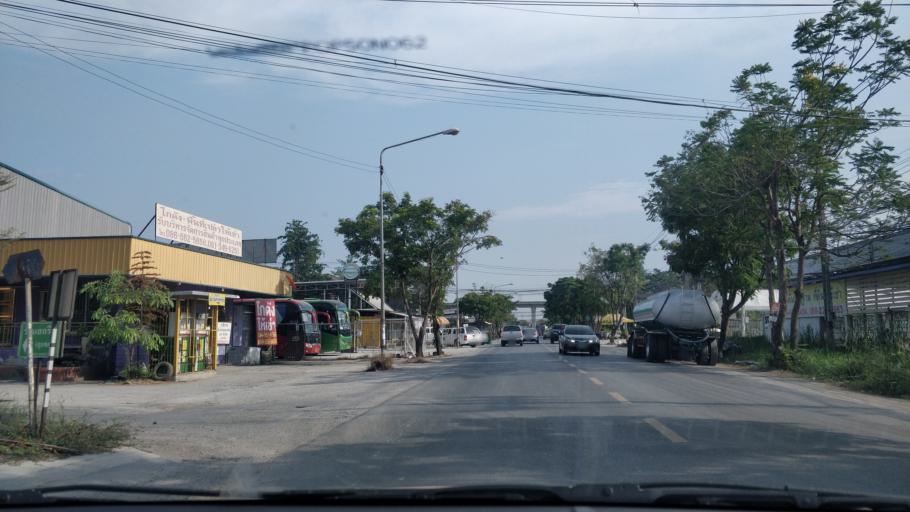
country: TH
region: Bangkok
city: Saphan Sung
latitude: 13.7347
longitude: 100.7162
